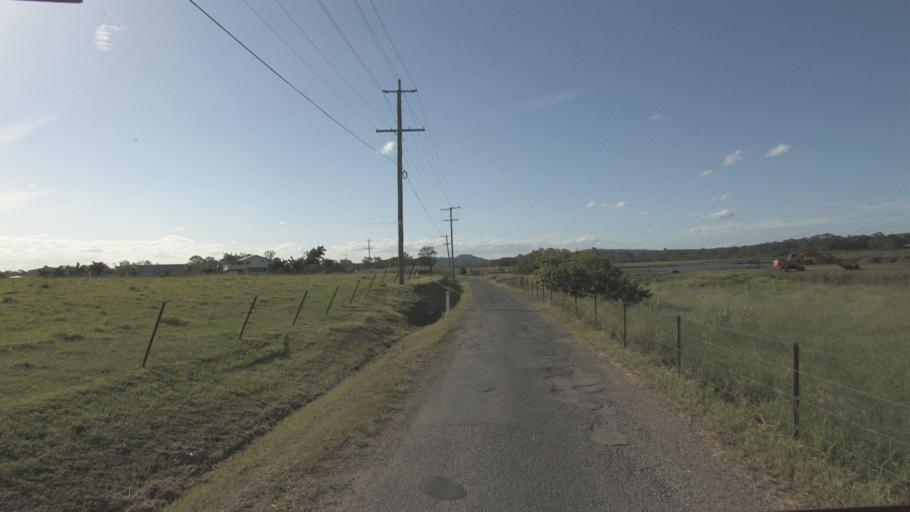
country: AU
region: Queensland
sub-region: Gold Coast
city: Yatala
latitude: -27.6917
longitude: 153.2369
